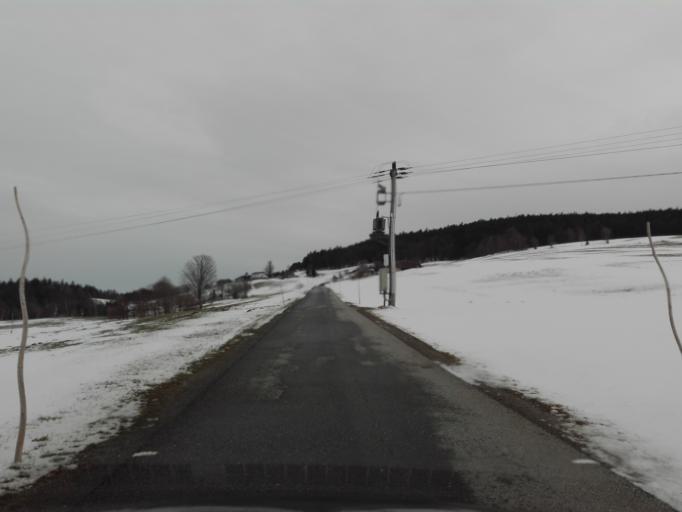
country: DE
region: Bavaria
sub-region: Lower Bavaria
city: Wegscheid
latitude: 48.5622
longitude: 13.8215
